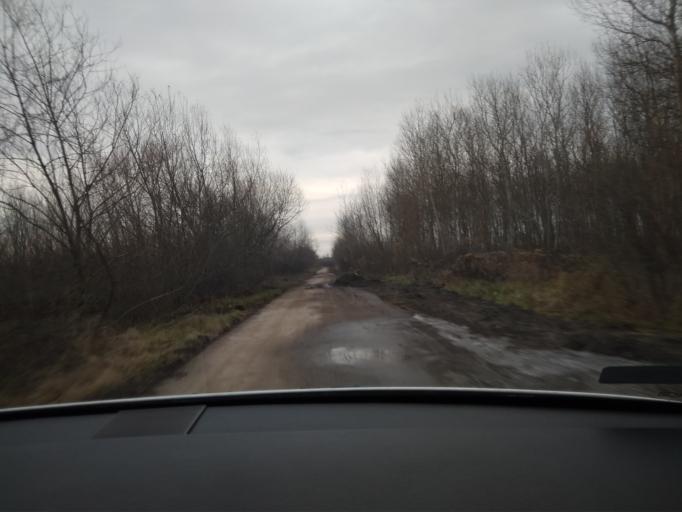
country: HU
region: Szabolcs-Szatmar-Bereg
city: Apagy
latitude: 47.9930
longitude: 21.8954
